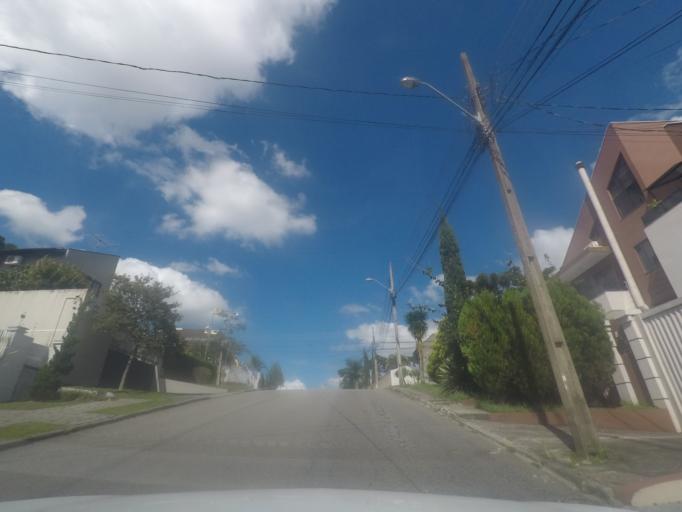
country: BR
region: Parana
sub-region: Pinhais
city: Pinhais
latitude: -25.4791
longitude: -49.2209
